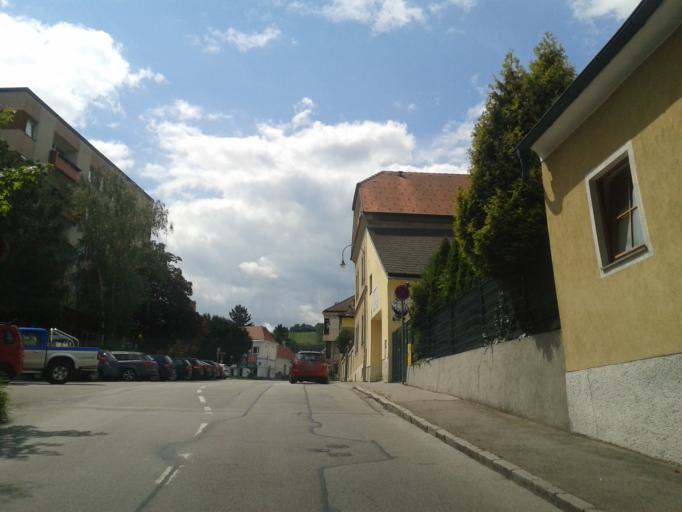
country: AT
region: Lower Austria
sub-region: Politischer Bezirk Wien-Umgebung
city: Klosterneuburg
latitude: 48.3043
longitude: 16.3272
